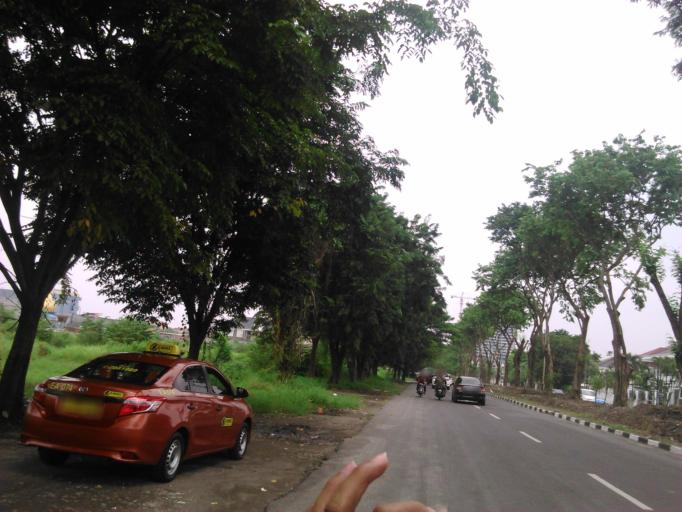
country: ID
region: East Java
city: Mulyorejo
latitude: -7.2796
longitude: 112.7891
